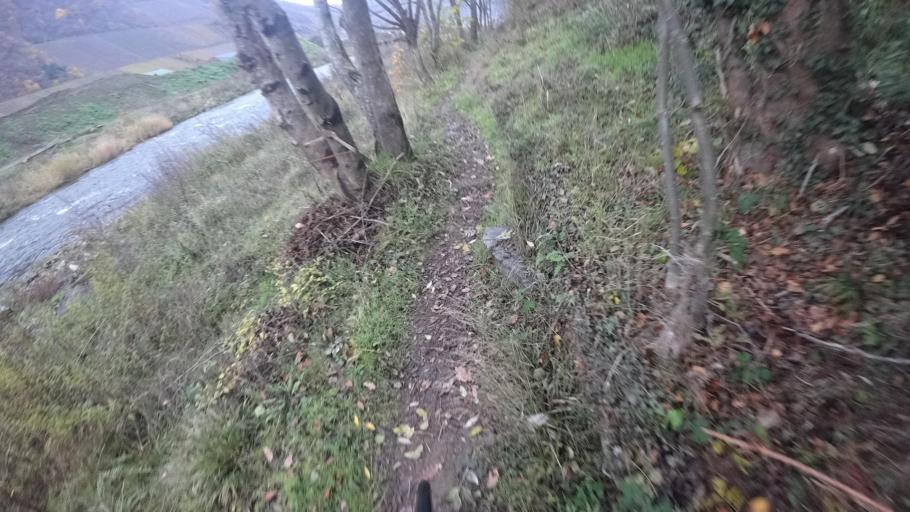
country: DE
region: Rheinland-Pfalz
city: Rech
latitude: 50.5235
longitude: 7.0417
